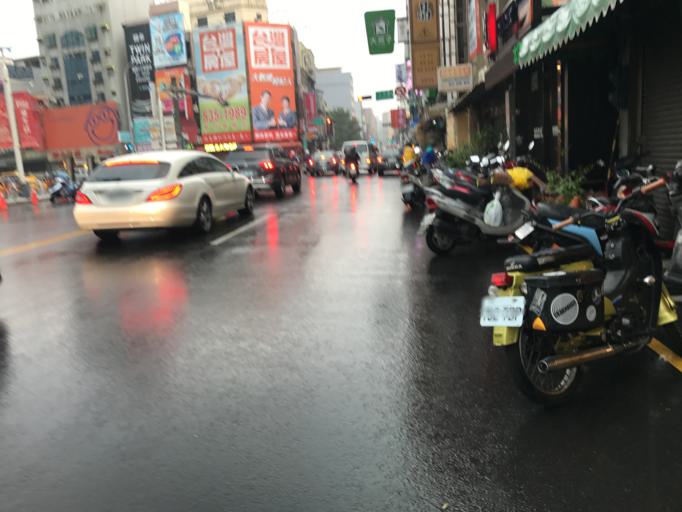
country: TW
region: Taiwan
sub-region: Hsinchu
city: Hsinchu
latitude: 24.8094
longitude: 120.9742
